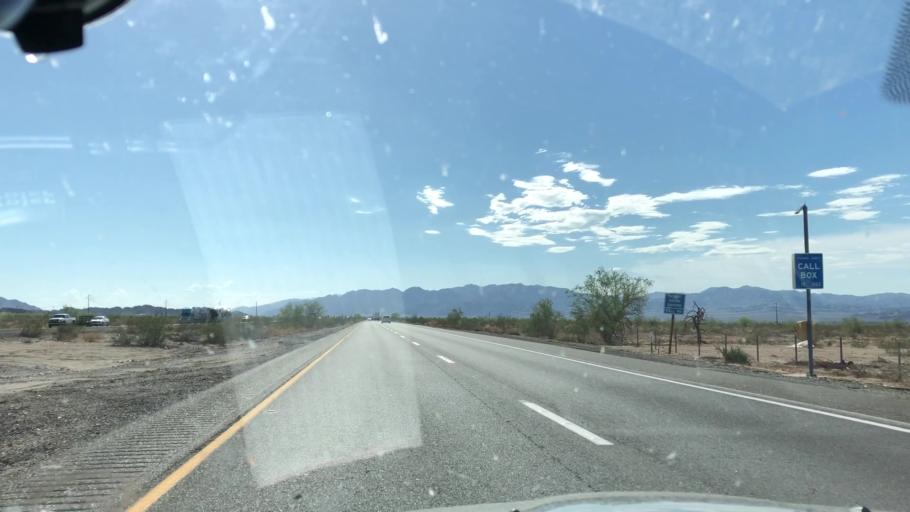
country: US
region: California
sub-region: Imperial County
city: Niland
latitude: 33.7070
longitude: -115.3494
